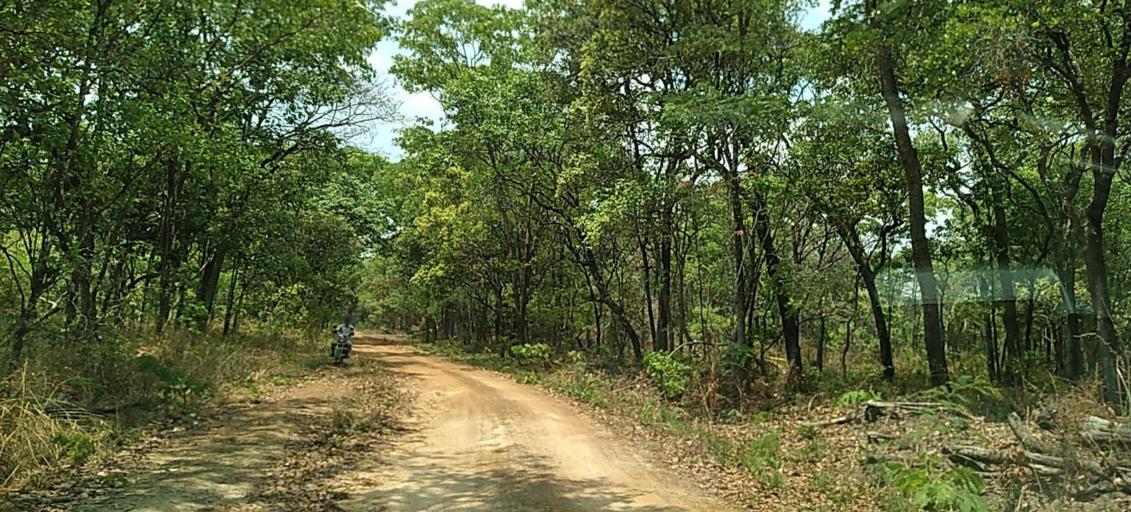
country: ZM
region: Copperbelt
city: Chingola
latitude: -12.7755
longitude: 27.6768
